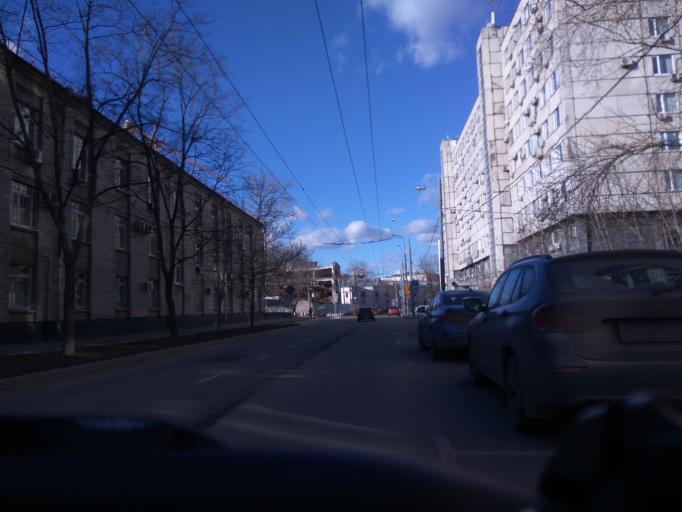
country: RU
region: Moscow
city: Mar'ina Roshcha
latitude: 55.8114
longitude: 37.6314
